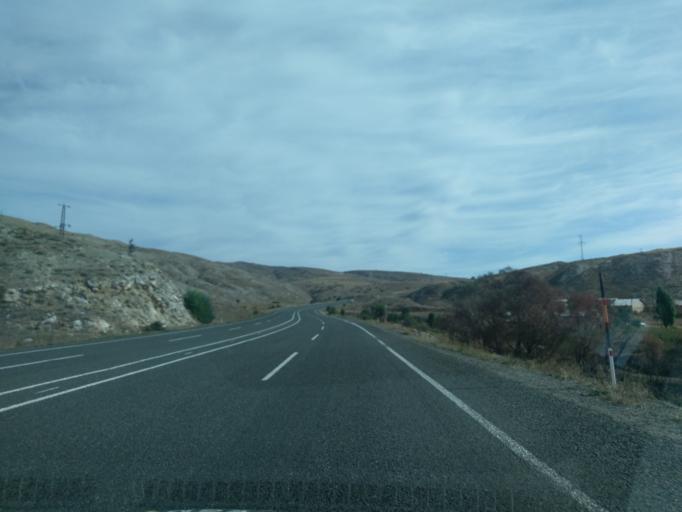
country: TR
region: Sivas
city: Zara
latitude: 39.8568
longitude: 37.8697
